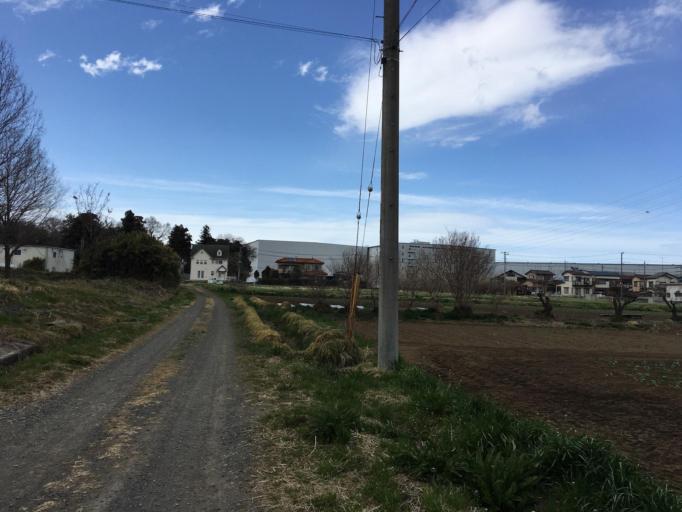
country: JP
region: Saitama
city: Ogawa
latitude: 36.1136
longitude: 139.2566
